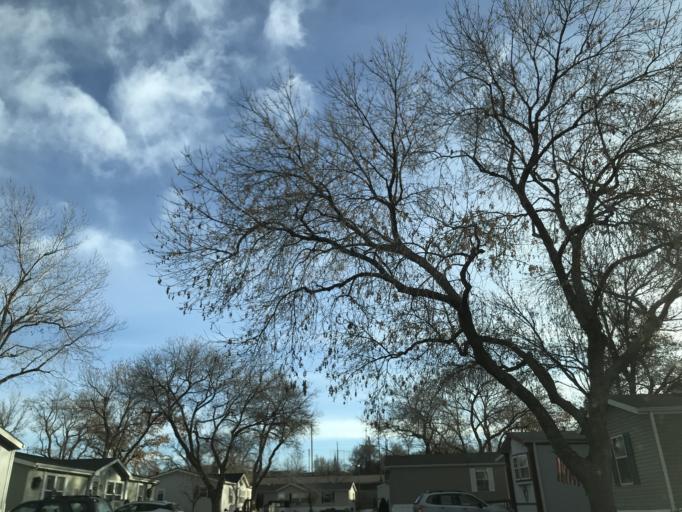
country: US
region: Colorado
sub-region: Arapahoe County
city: Columbine Valley
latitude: 39.5953
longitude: -105.0230
